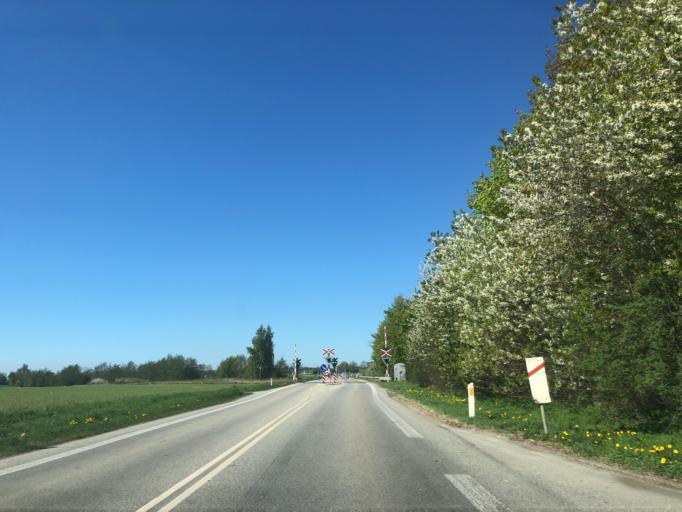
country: DK
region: Zealand
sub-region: Stevns Kommune
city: Store Heddinge
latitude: 55.3220
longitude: 12.3665
